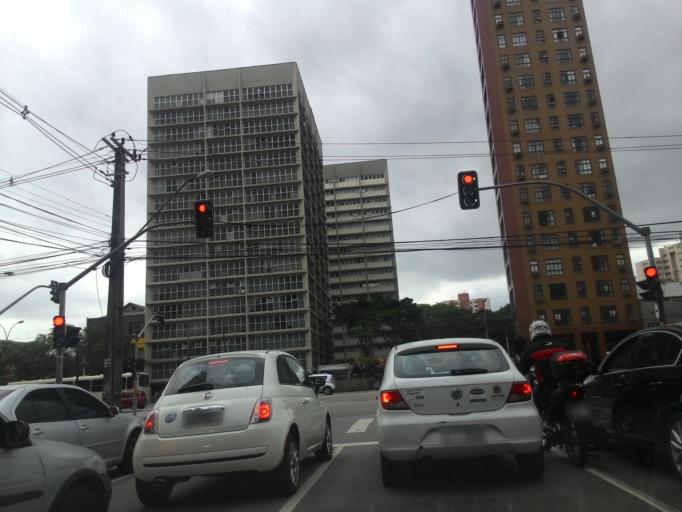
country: BR
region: Parana
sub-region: Curitiba
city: Curitiba
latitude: -25.4204
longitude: -49.2687
